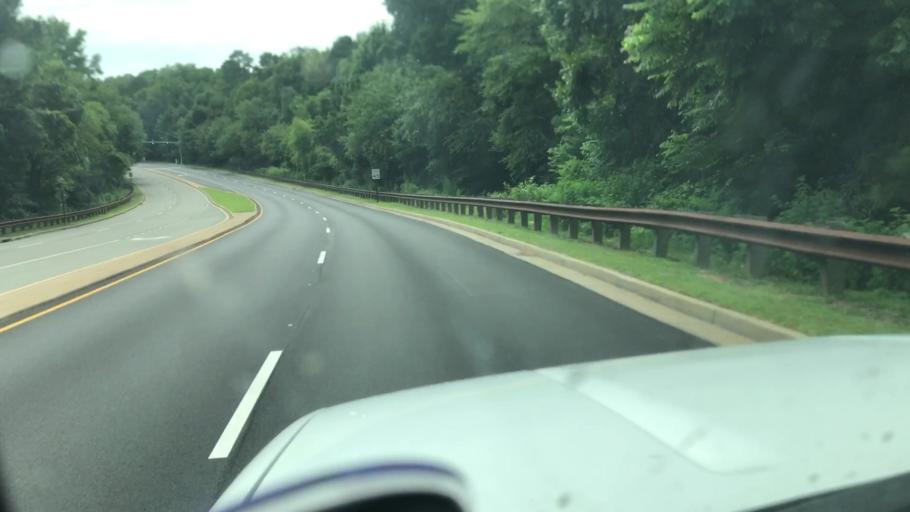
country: US
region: Virginia
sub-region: Henrico County
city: Short Pump
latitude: 37.6256
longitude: -77.5986
